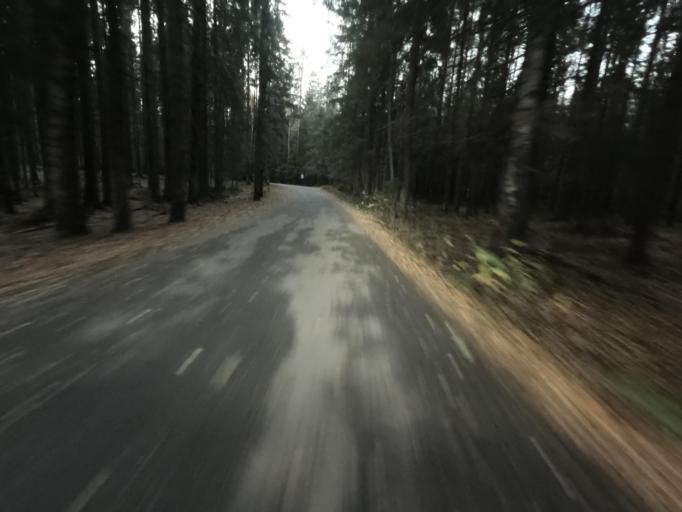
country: RU
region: St.-Petersburg
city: Komarovo
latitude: 60.2071
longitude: 29.7987
